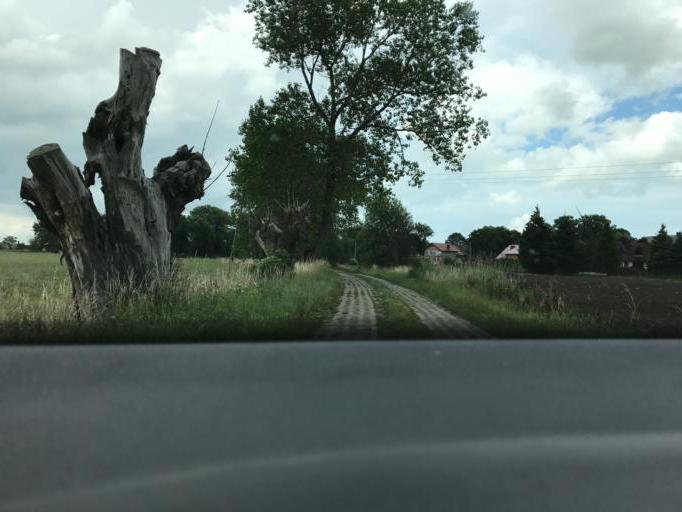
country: PL
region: Pomeranian Voivodeship
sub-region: Gdansk
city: Gdansk
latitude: 54.3096
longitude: 18.7256
